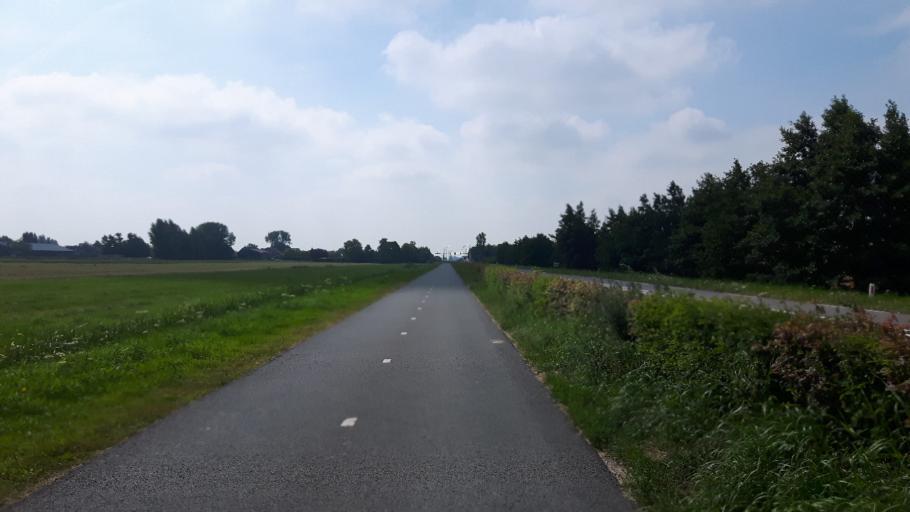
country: NL
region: Utrecht
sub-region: Gemeente Montfoort
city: Montfoort
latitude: 52.0101
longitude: 4.9600
